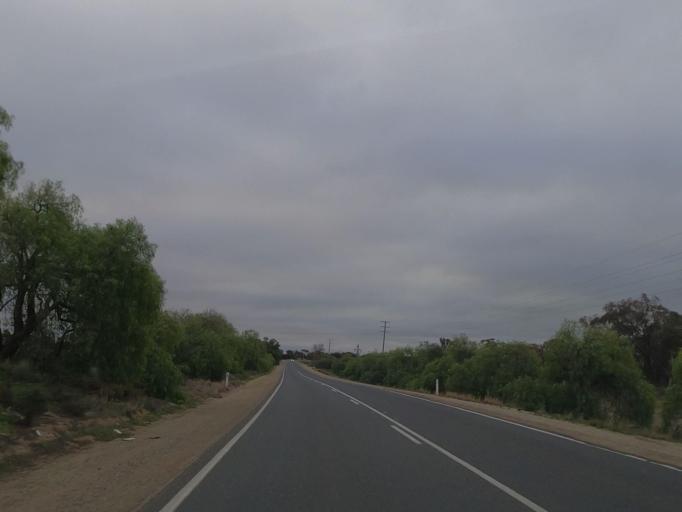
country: AU
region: Victoria
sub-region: Swan Hill
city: Swan Hill
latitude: -35.4453
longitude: 143.6194
